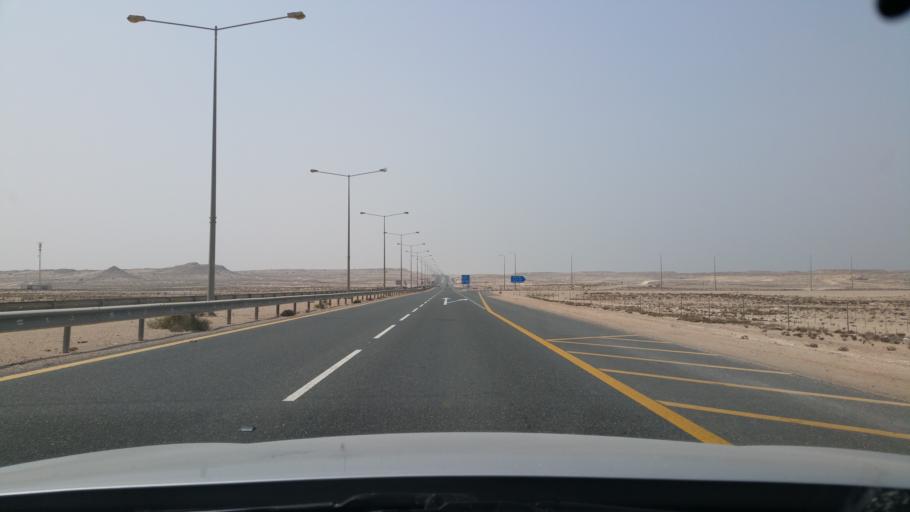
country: QA
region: Baladiyat ar Rayyan
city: Dukhan
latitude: 25.3741
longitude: 50.7808
